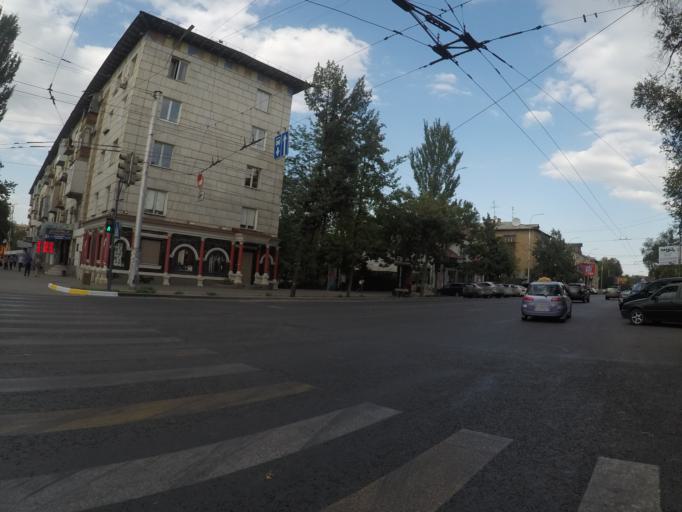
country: KG
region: Chuy
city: Bishkek
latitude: 42.8753
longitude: 74.5884
